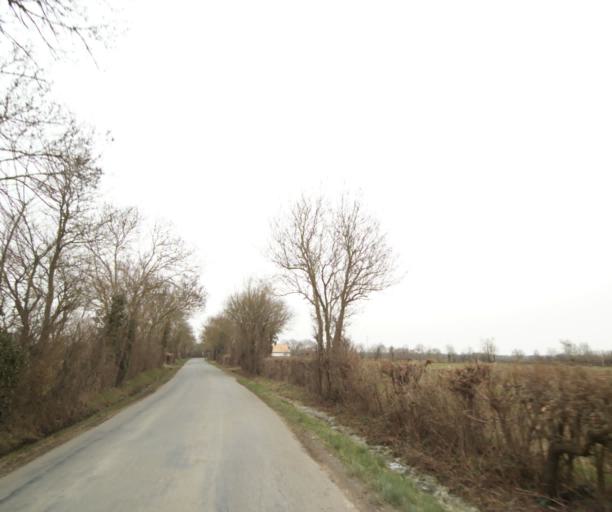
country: FR
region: Poitou-Charentes
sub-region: Departement des Deux-Sevres
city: Bessines
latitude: 46.2956
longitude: -0.4822
